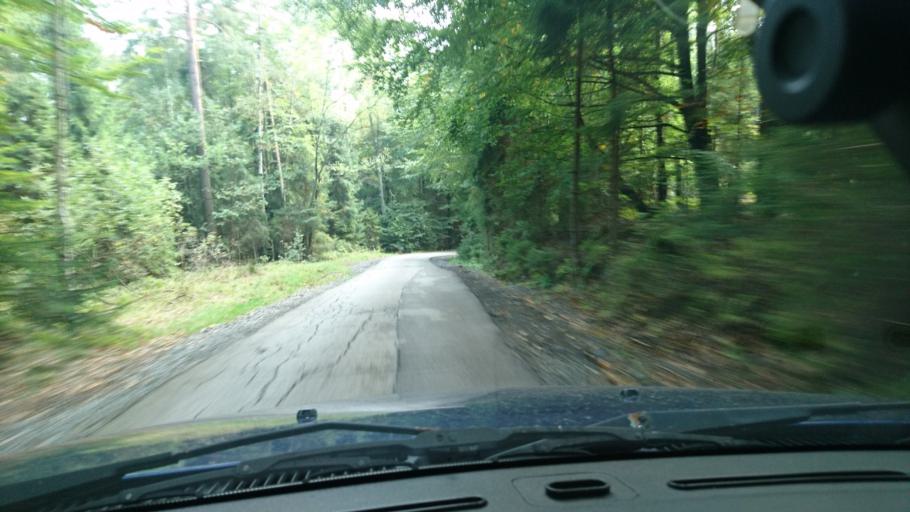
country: PL
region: Silesian Voivodeship
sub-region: Powiat bielski
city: Wilkowice
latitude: 49.7685
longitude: 19.1177
